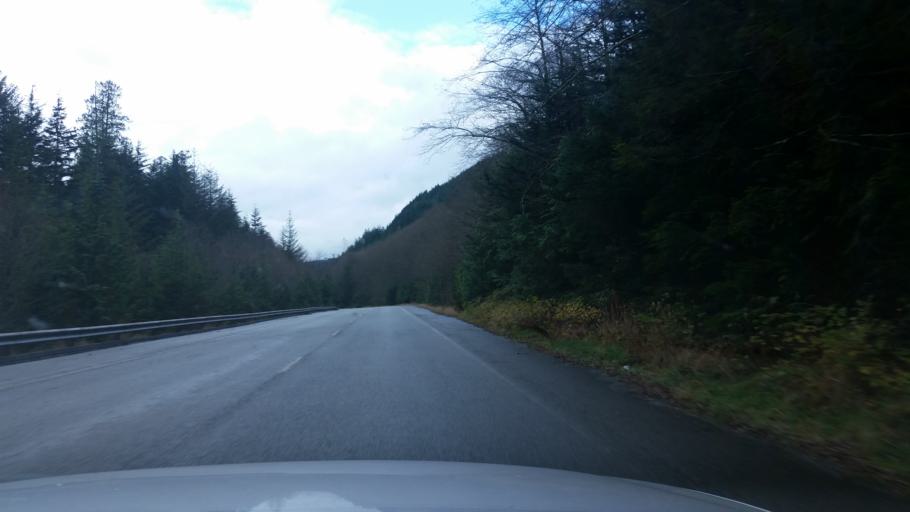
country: US
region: Washington
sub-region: King County
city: Tanner
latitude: 47.4348
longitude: -121.6532
